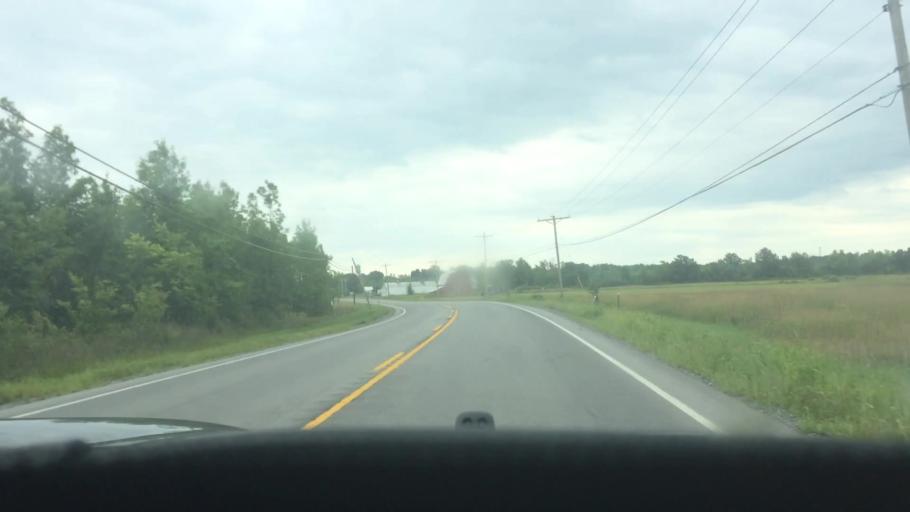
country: US
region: New York
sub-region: St. Lawrence County
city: Ogdensburg
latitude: 44.6285
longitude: -75.4210
